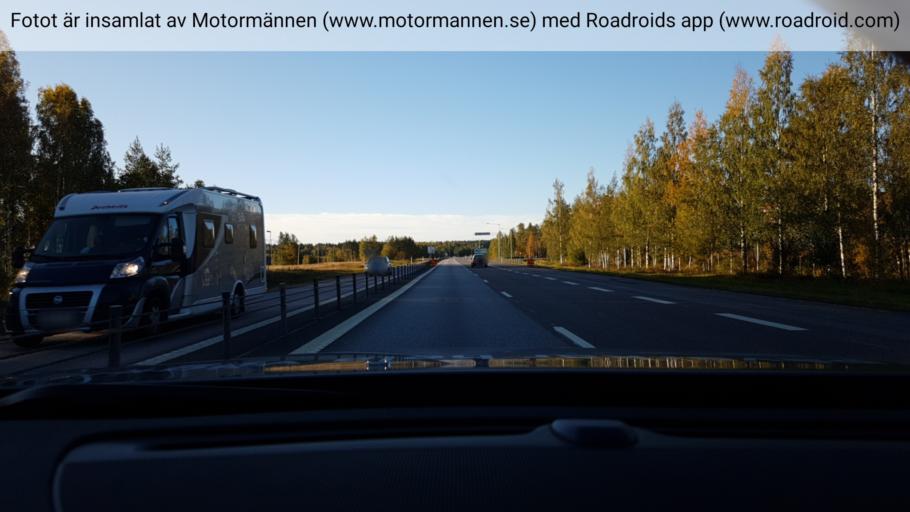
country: SE
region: Norrbotten
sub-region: Lulea Kommun
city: Gammelstad
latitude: 65.6162
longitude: 22.0558
